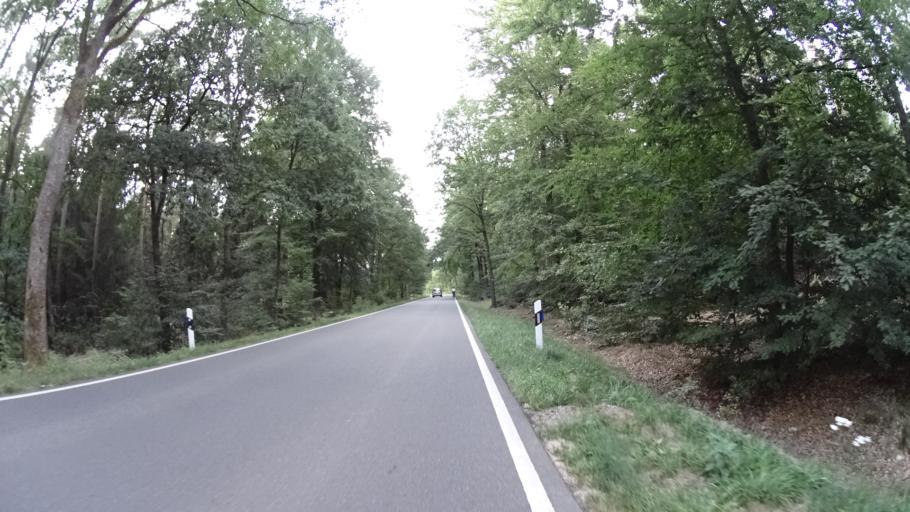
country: DE
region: Lower Saxony
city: Undeloh
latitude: 53.1679
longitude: 9.8947
